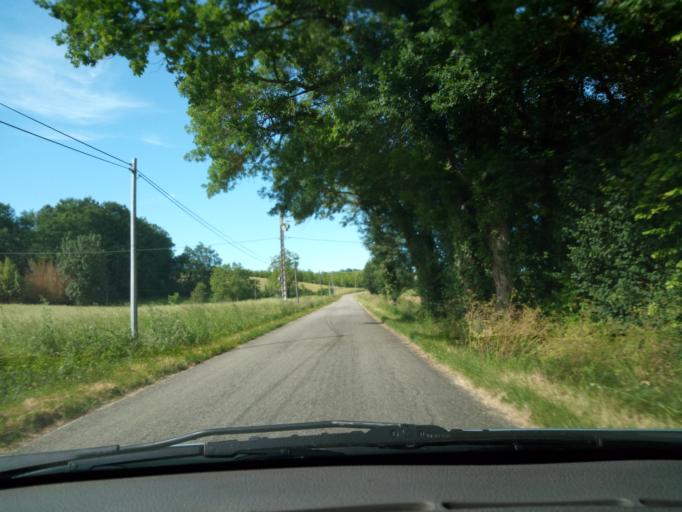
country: FR
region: Midi-Pyrenees
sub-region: Departement du Tarn-et-Garonne
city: Molieres
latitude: 44.2307
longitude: 1.3295
